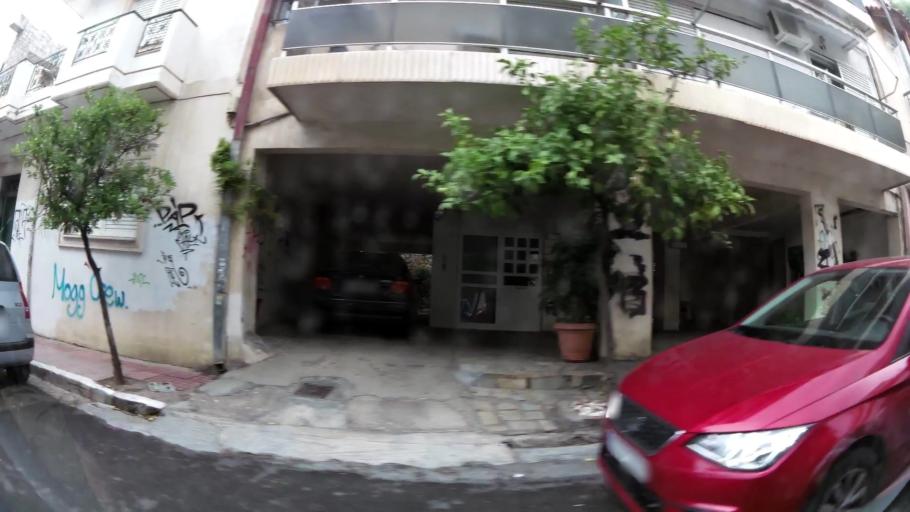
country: GR
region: Attica
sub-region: Nomarchia Athinas
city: Kaisariani
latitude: 37.9577
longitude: 23.7640
